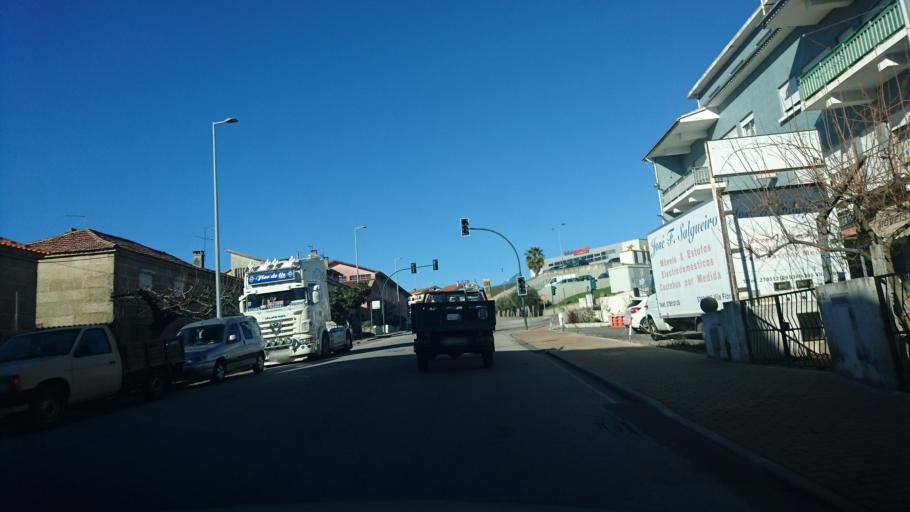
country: PT
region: Braganca
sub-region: Braganca Municipality
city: Vila Flor
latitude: 41.3091
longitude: -7.1615
